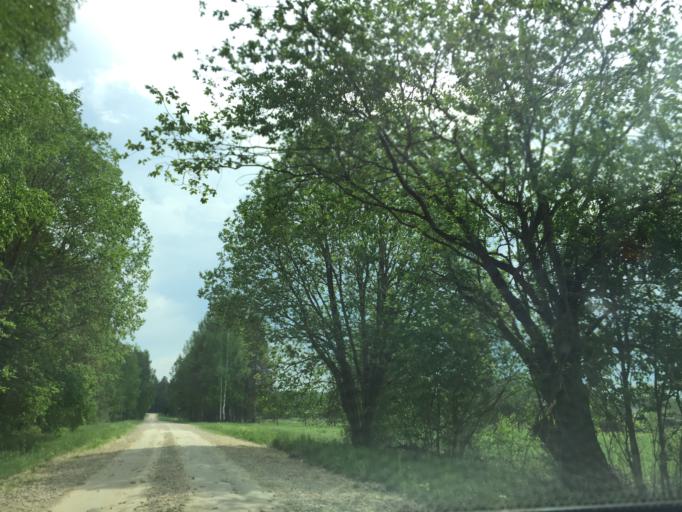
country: LV
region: Livani
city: Livani
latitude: 56.5720
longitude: 26.2145
